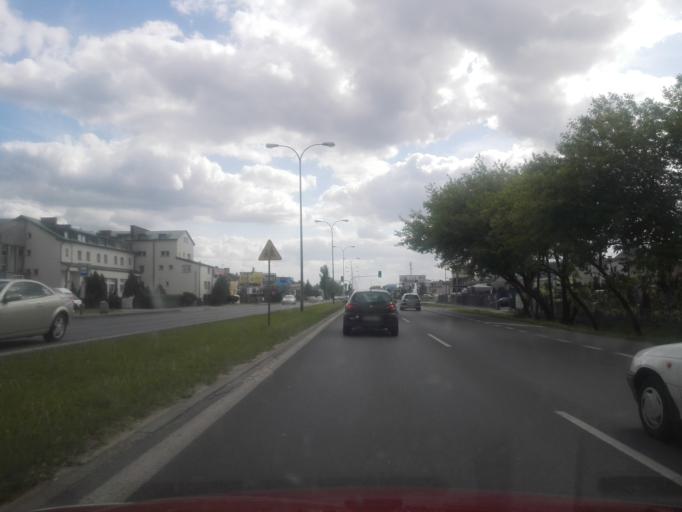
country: PL
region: Masovian Voivodeship
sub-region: Powiat wolominski
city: Zabki
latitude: 52.2920
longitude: 21.0794
